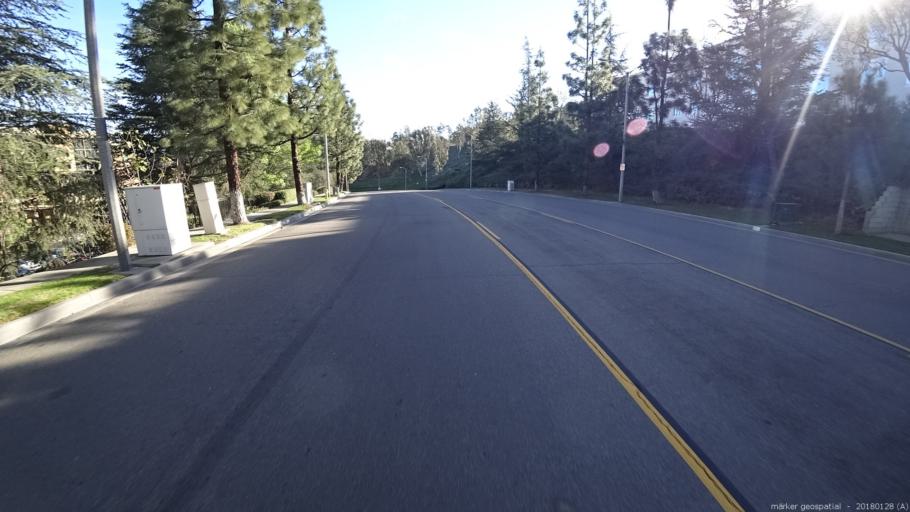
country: US
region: California
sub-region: Los Angeles County
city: Diamond Bar
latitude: 34.0001
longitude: -117.8340
